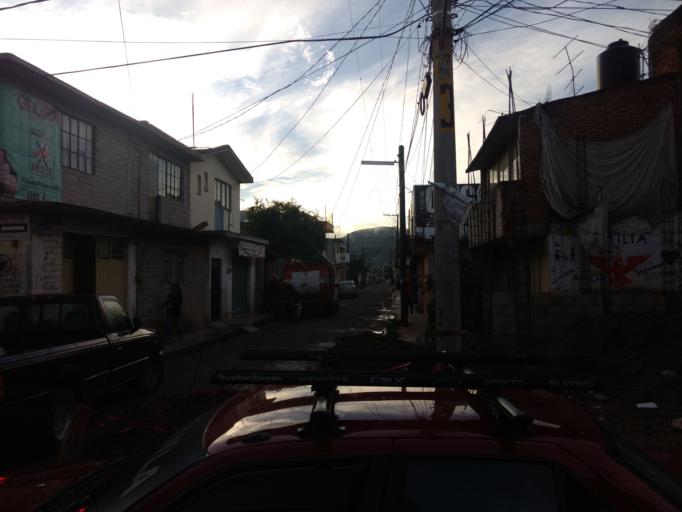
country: MX
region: Oaxaca
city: Ciudad de Huajuapam de Leon
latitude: 17.8092
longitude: -97.7792
